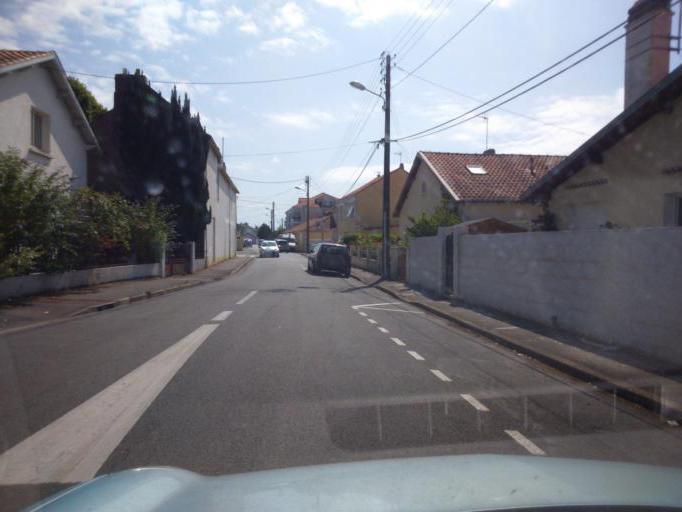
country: FR
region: Pays de la Loire
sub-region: Departement de la Loire-Atlantique
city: Saint-Sebastien-sur-Loire
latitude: 47.1987
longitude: -1.5163
